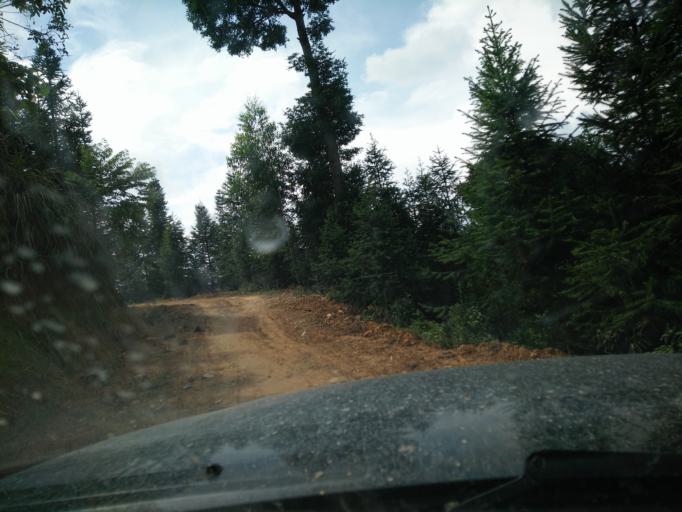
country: CN
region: Guangxi Zhuangzu Zizhiqu
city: Leli
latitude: 24.7744
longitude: 105.9101
